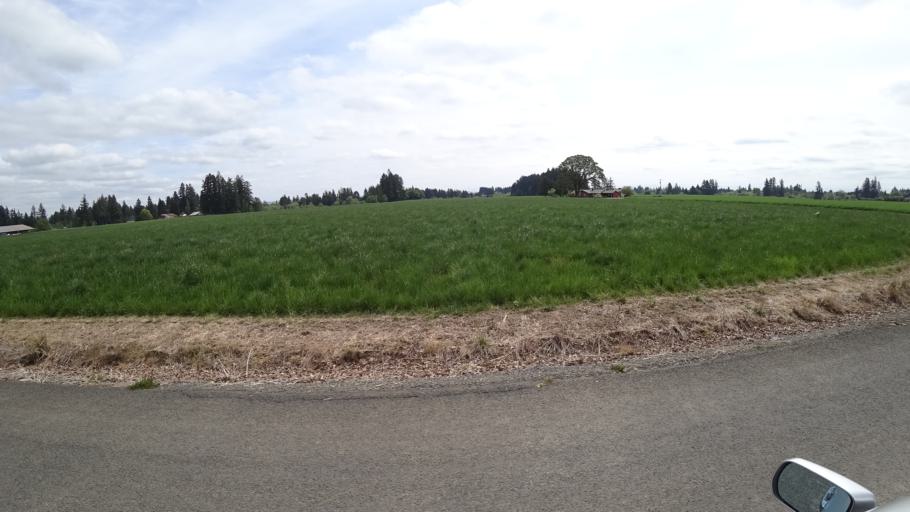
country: US
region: Oregon
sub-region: Washington County
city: Hillsboro
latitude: 45.5400
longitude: -123.0130
